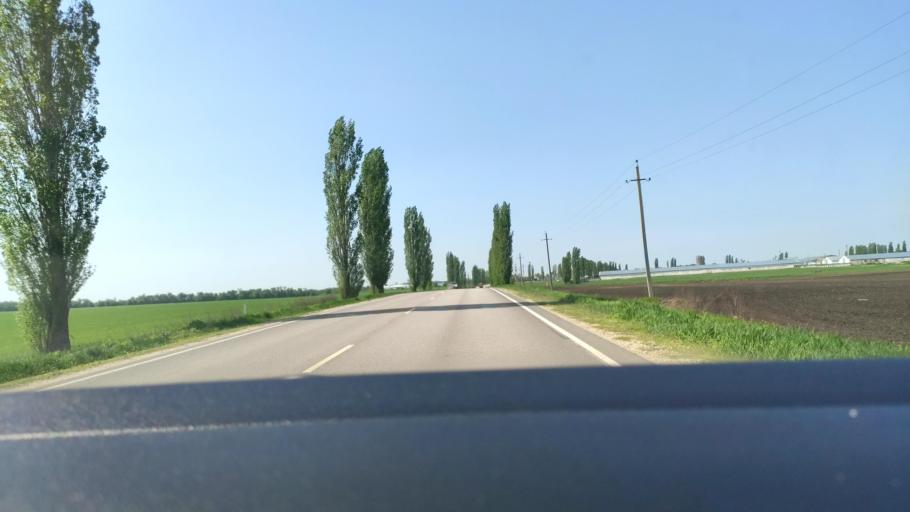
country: RU
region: Voronezj
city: Novaya Usman'
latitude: 51.5500
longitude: 39.3668
